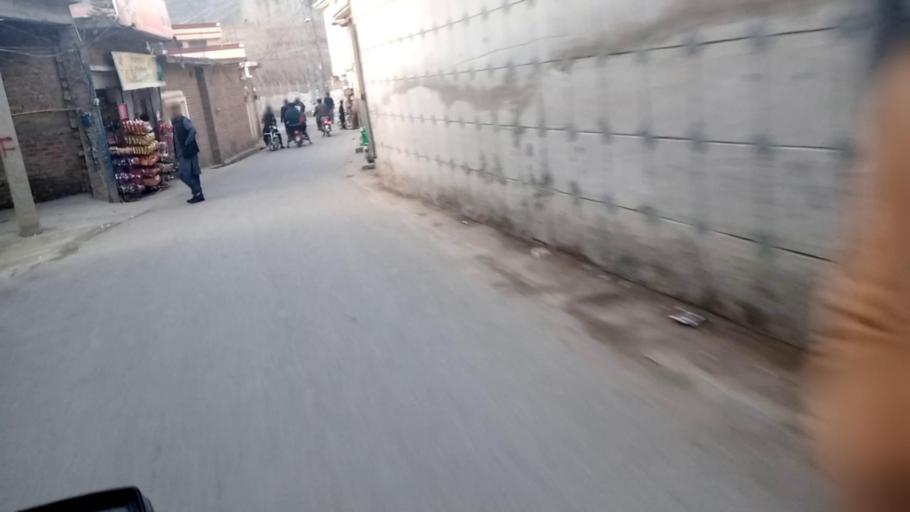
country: PK
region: Khyber Pakhtunkhwa
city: Saidu Sharif
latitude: 34.7461
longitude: 72.3507
